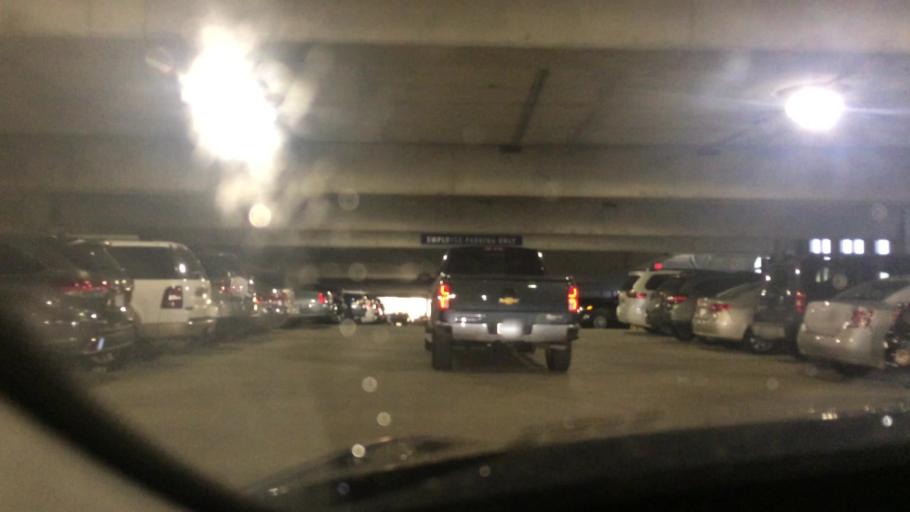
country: US
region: Ohio
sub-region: Hancock County
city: Findlay
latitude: 41.0344
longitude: -83.6483
